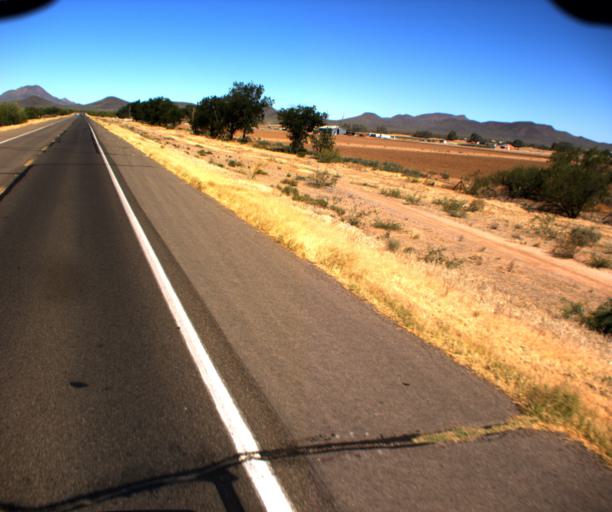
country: US
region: Arizona
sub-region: Pima County
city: Three Points
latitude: 32.0758
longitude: -111.3236
